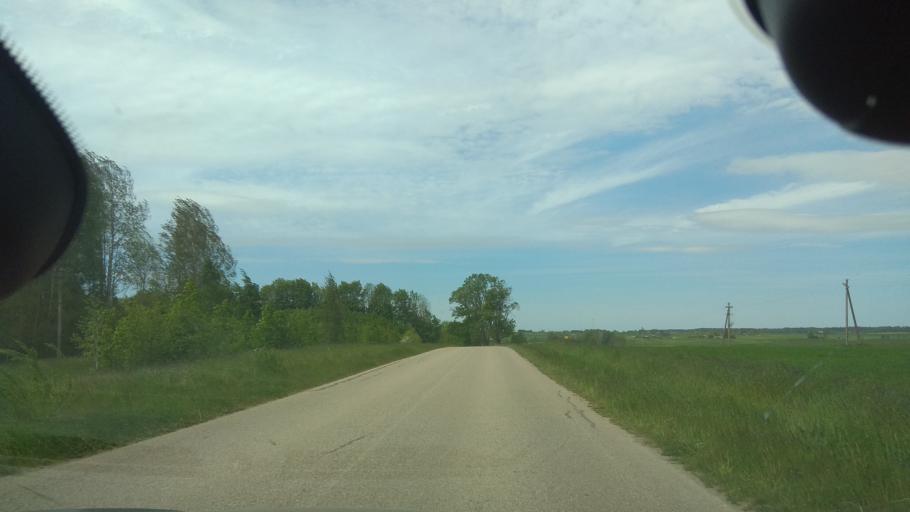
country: LT
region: Vilnius County
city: Ukmerge
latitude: 55.1493
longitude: 24.5584
